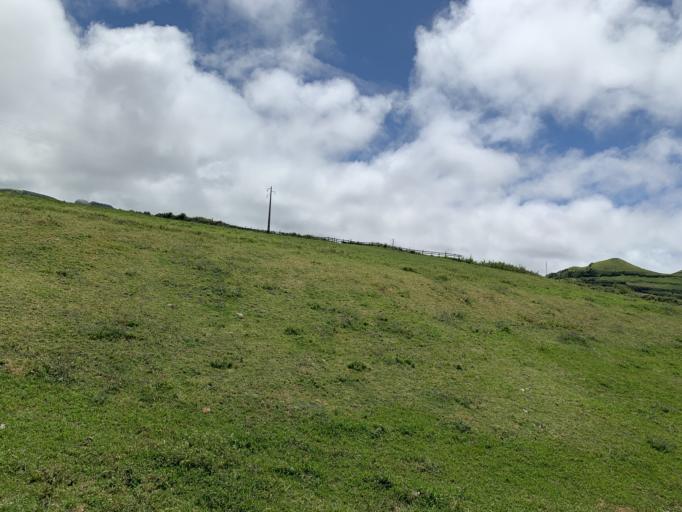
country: PT
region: Azores
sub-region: Ponta Delgada
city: Arrifes
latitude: 37.8571
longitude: -25.8504
